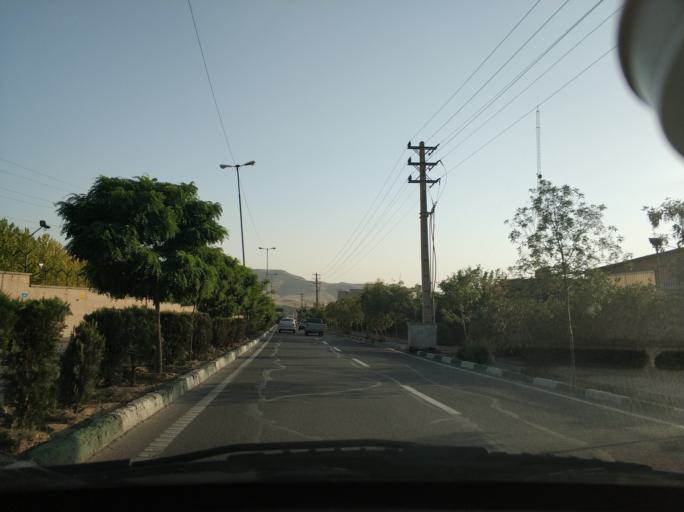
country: IR
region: Tehran
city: Tehran
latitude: 35.7302
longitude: 51.5933
